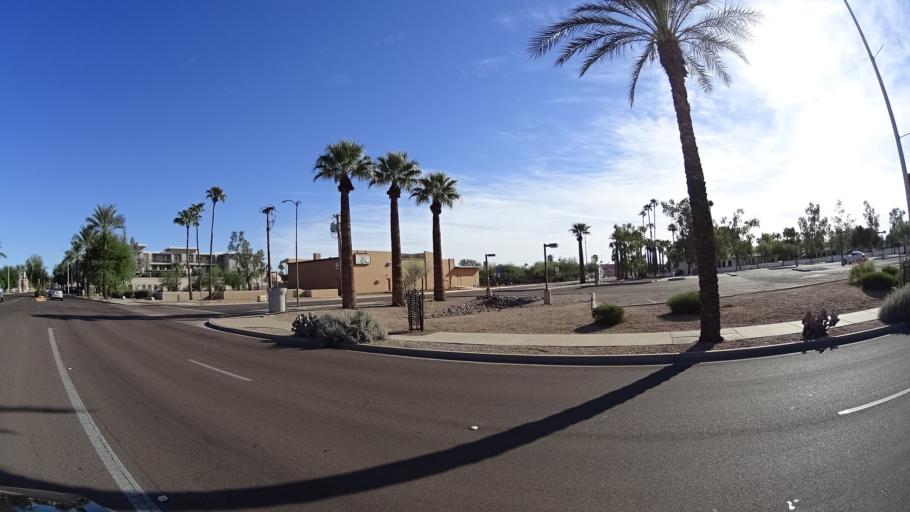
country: US
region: Arizona
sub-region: Maricopa County
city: Scottsdale
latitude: 33.4909
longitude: -111.9302
